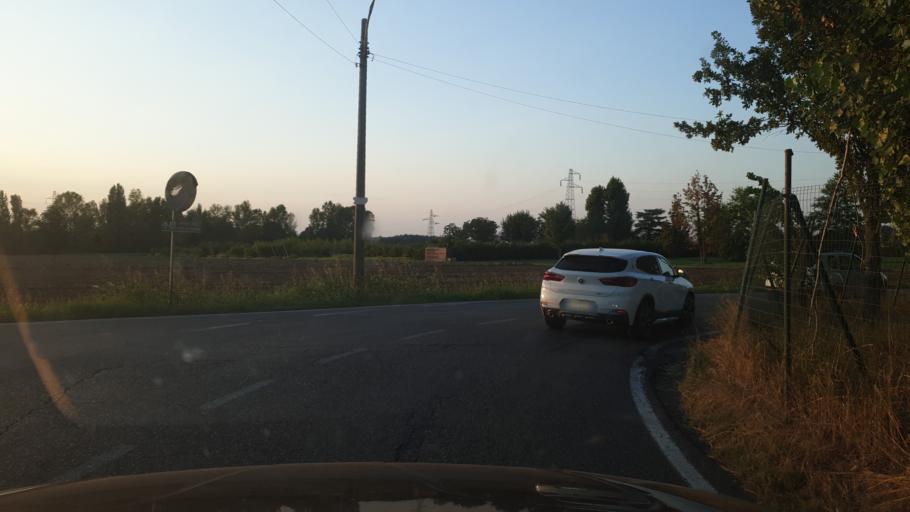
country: IT
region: Emilia-Romagna
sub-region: Provincia di Bologna
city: Quarto Inferiore
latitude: 44.5246
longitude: 11.3790
